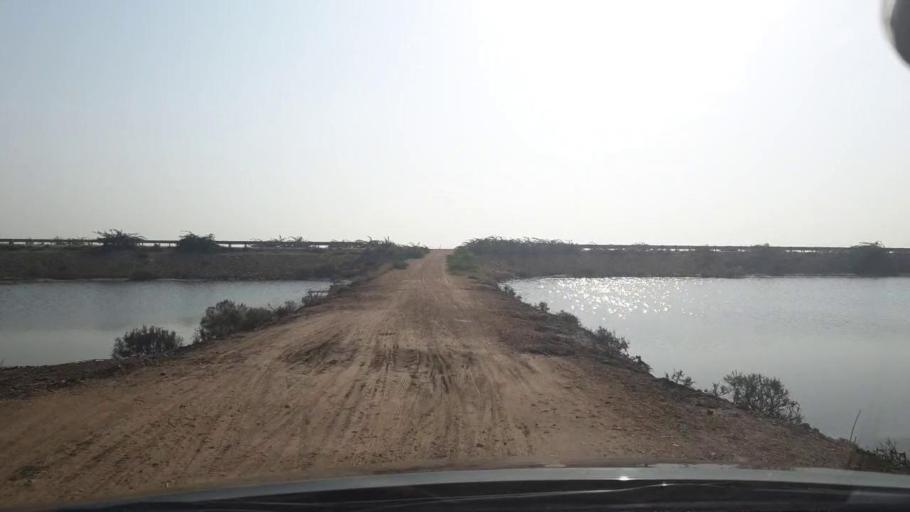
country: PK
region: Sindh
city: Tando Bago
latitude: 24.6511
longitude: 69.1298
